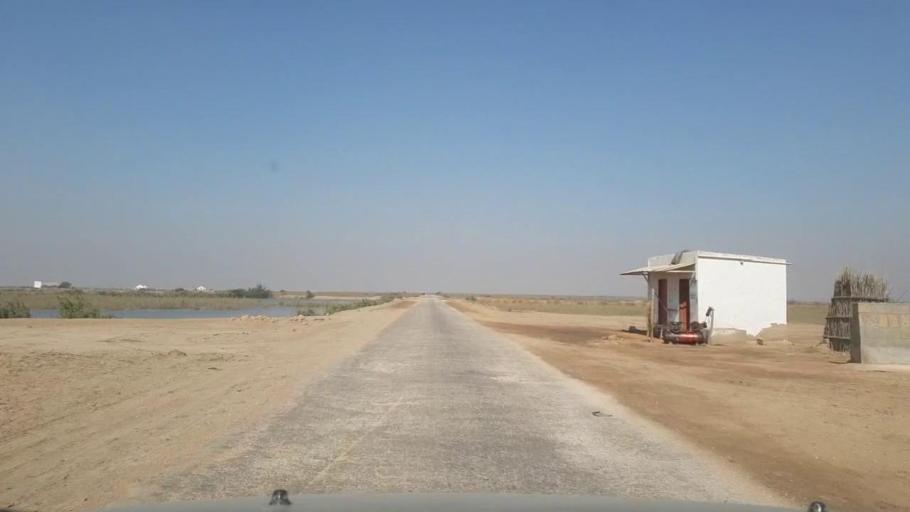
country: PK
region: Sindh
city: Thatta
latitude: 24.8146
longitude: 67.8971
